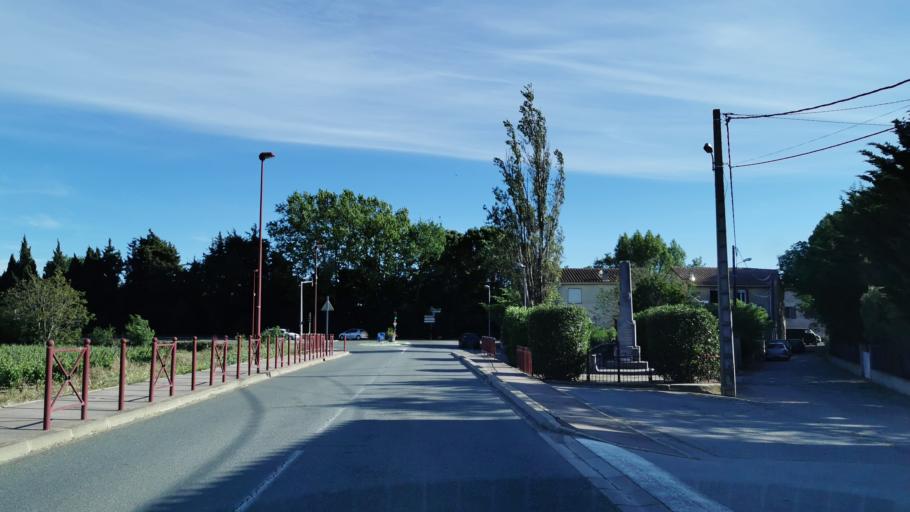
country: FR
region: Languedoc-Roussillon
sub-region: Departement de l'Aude
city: Canet
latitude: 43.2150
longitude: 2.8629
